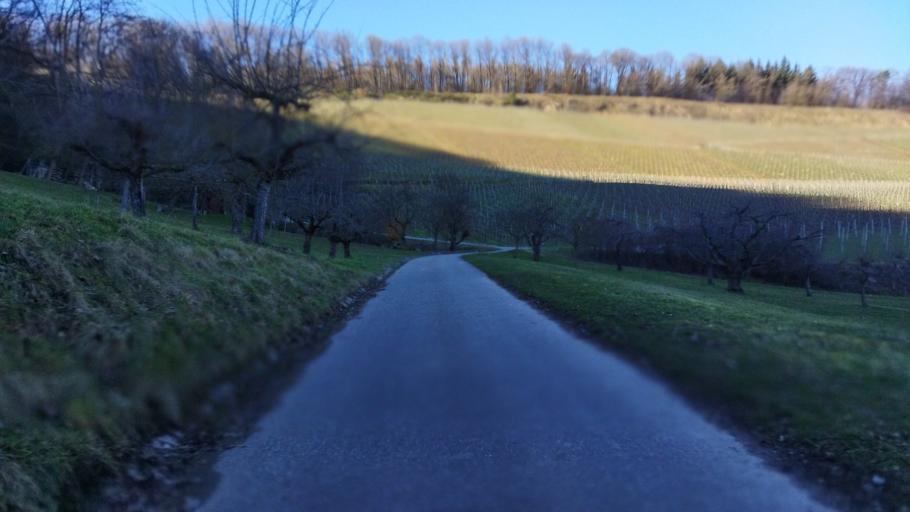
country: DE
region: Baden-Wuerttemberg
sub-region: Regierungsbezirk Stuttgart
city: Erlenbach
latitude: 49.1738
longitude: 9.2850
